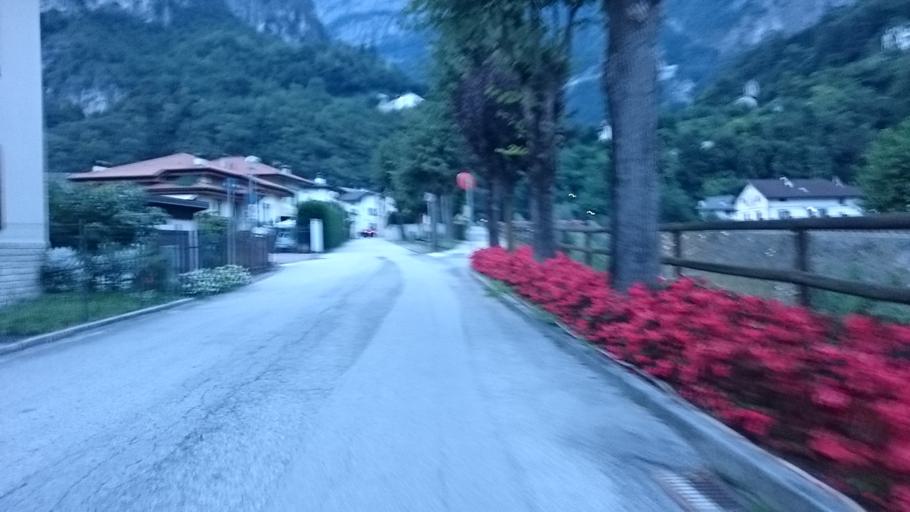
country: IT
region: Trentino-Alto Adige
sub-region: Provincia di Trento
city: Grigno
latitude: 46.0157
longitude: 11.6366
